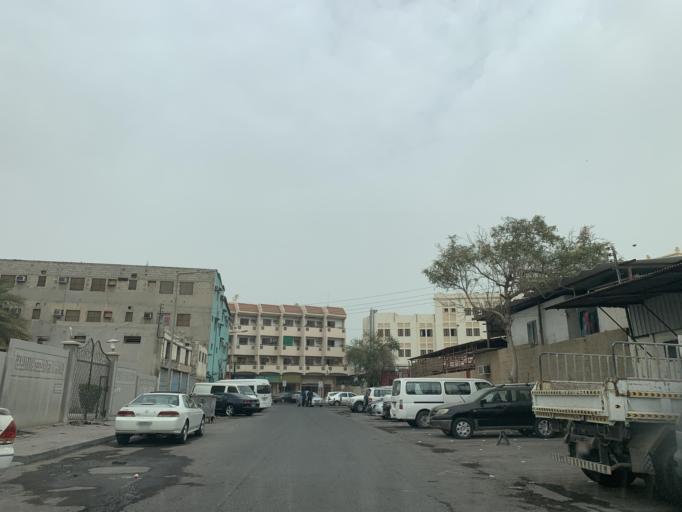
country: BH
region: Manama
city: Manama
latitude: 26.2268
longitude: 50.5808
